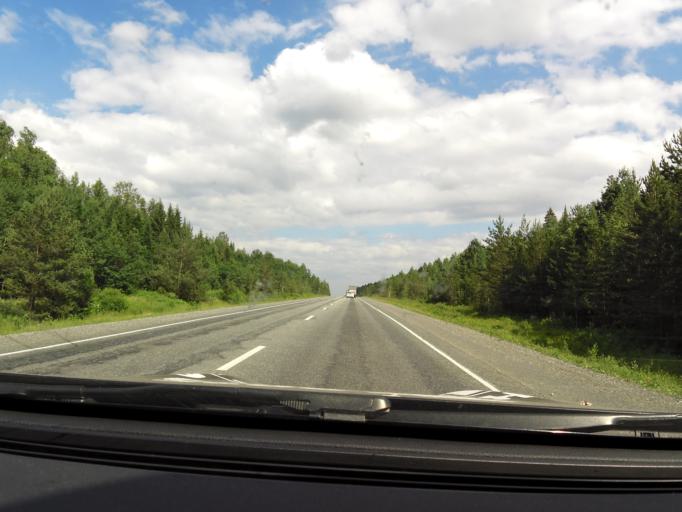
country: RU
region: Sverdlovsk
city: Nizhniye Sergi
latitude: 56.8253
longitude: 59.2376
